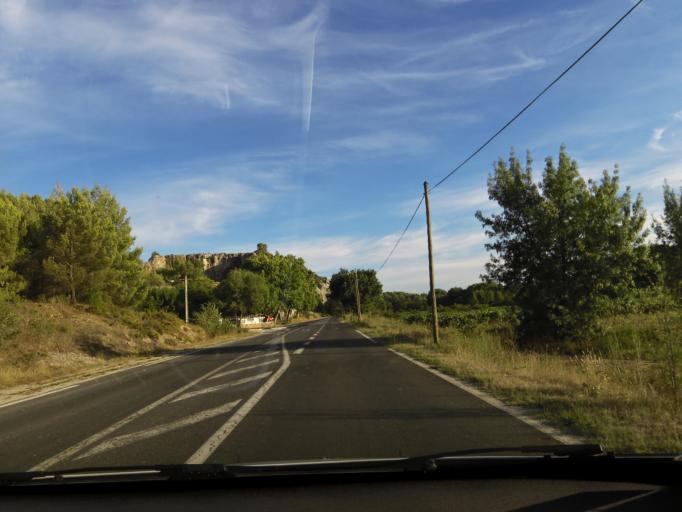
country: FR
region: Languedoc-Roussillon
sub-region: Departement de l'Herault
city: Prades-le-Lez
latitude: 43.7102
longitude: 3.8674
